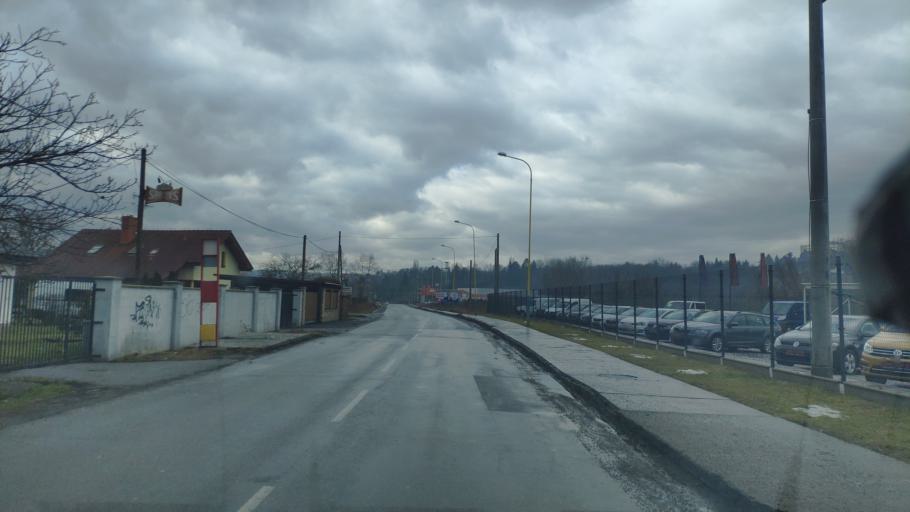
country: SK
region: Presovsky
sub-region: Okres Presov
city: Presov
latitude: 48.9931
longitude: 21.2649
